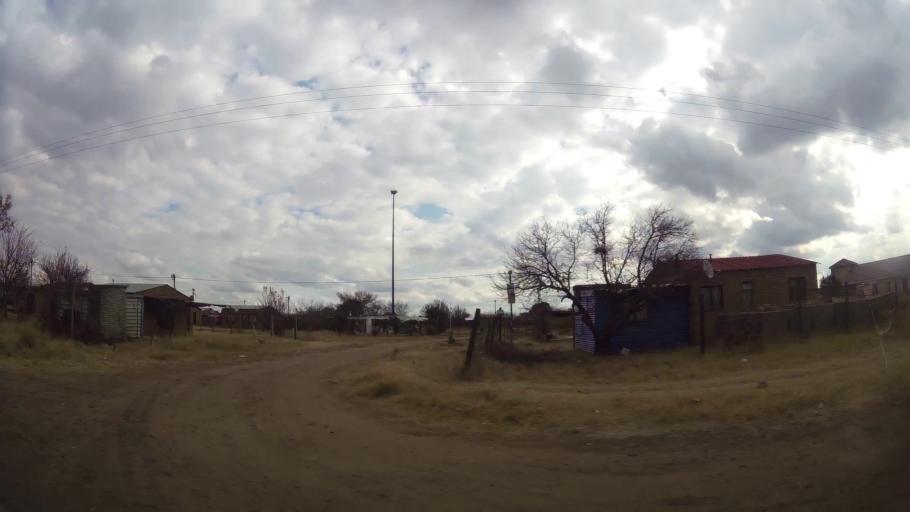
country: ZA
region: Orange Free State
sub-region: Fezile Dabi District Municipality
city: Sasolburg
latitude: -26.8578
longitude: 27.8529
